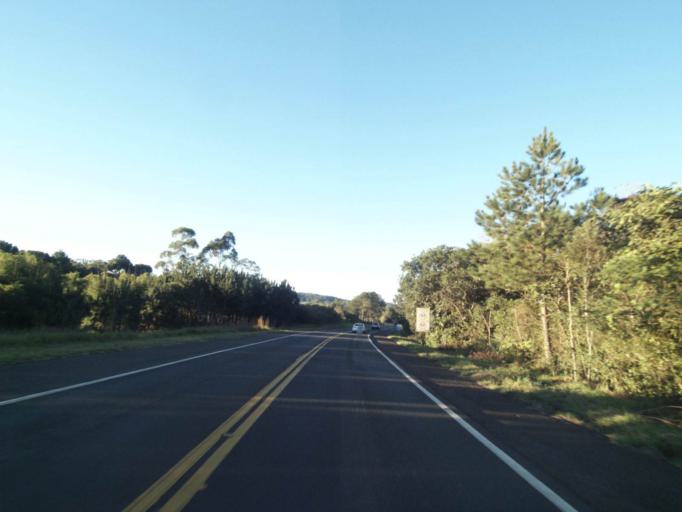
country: BR
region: Parana
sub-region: Faxinal
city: Faxinal
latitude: -23.8913
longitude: -51.1862
